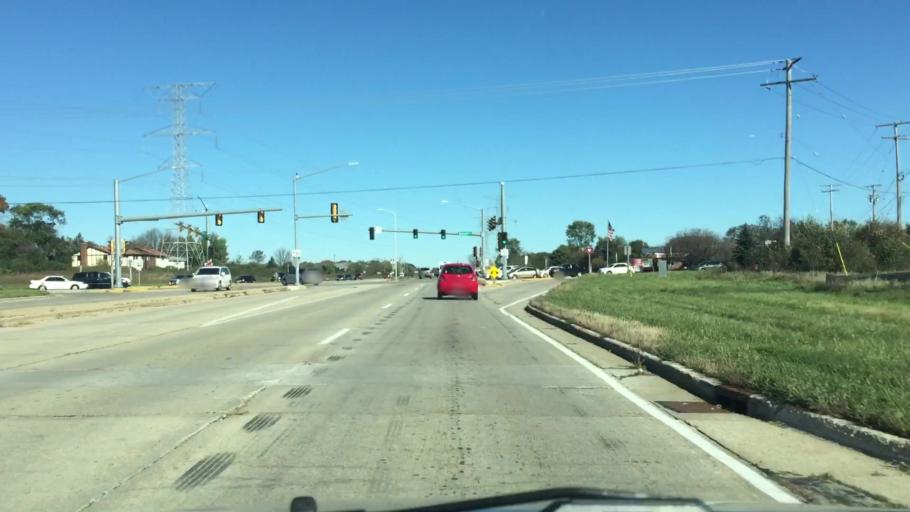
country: US
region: Wisconsin
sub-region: Waukesha County
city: Waukesha
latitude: 42.9856
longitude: -88.2081
